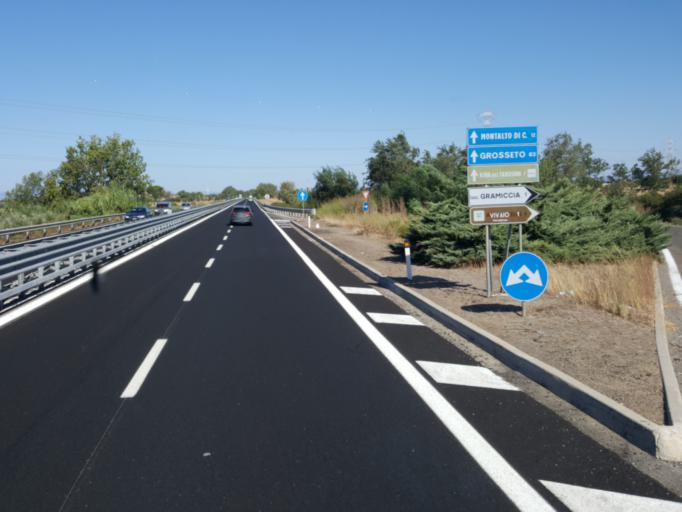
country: IT
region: Latium
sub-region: Provincia di Viterbo
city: Tarquinia
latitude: 42.2776
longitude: 11.7016
